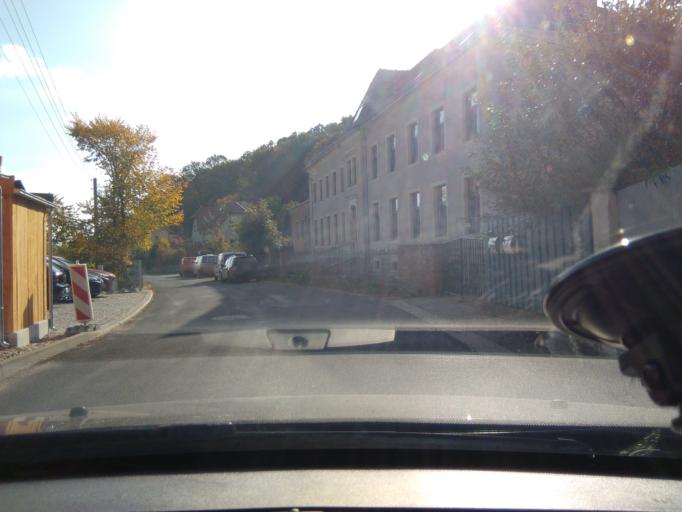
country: DE
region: Saxony
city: Meissen
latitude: 51.1518
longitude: 13.5132
